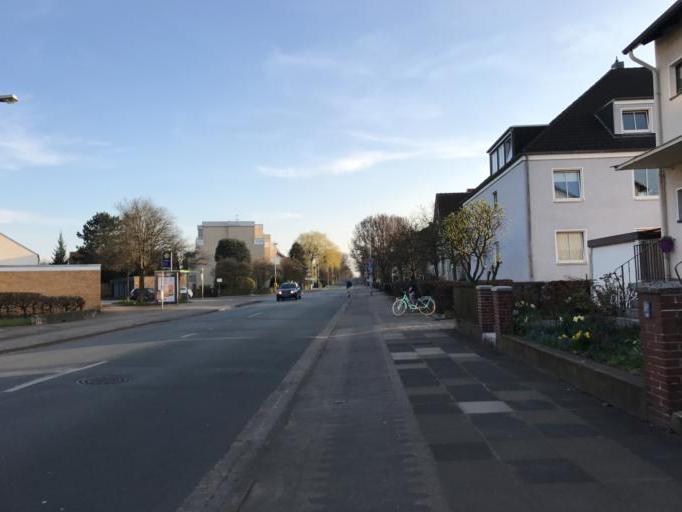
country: DE
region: Lower Saxony
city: Laatzen
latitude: 52.3480
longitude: 9.7815
